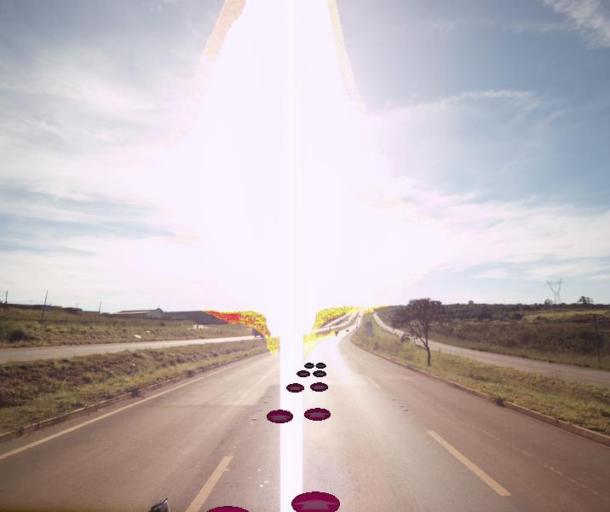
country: BR
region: Federal District
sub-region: Brasilia
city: Brasilia
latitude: -15.7410
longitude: -48.3122
